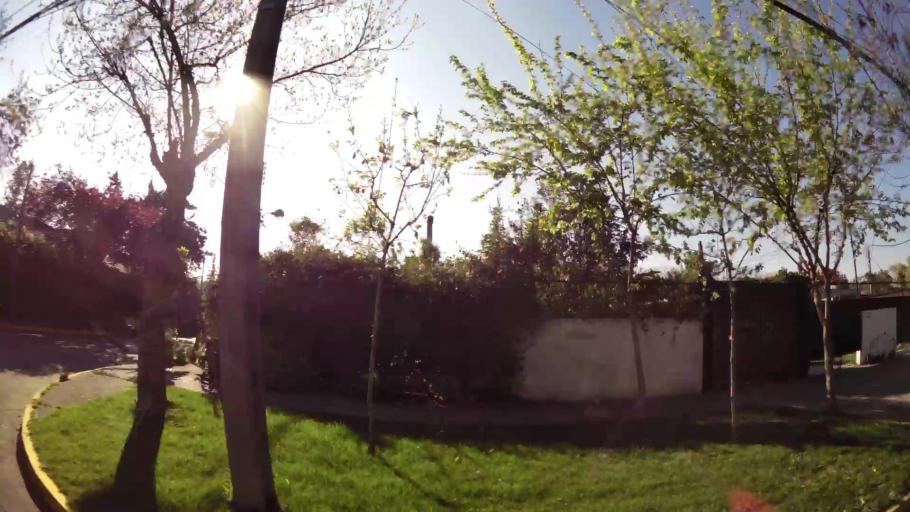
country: CL
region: Santiago Metropolitan
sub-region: Provincia de Santiago
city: Villa Presidente Frei, Nunoa, Santiago, Chile
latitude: -33.4475
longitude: -70.5848
